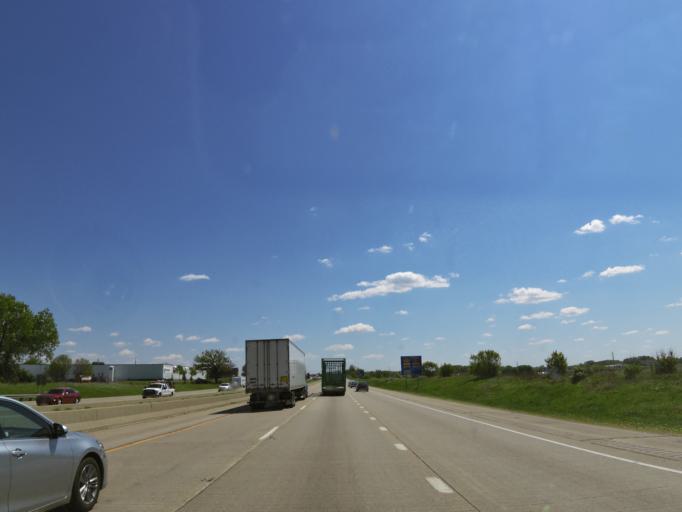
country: US
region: Wisconsin
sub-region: Dane County
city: McFarland
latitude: 43.0602
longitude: -89.2772
